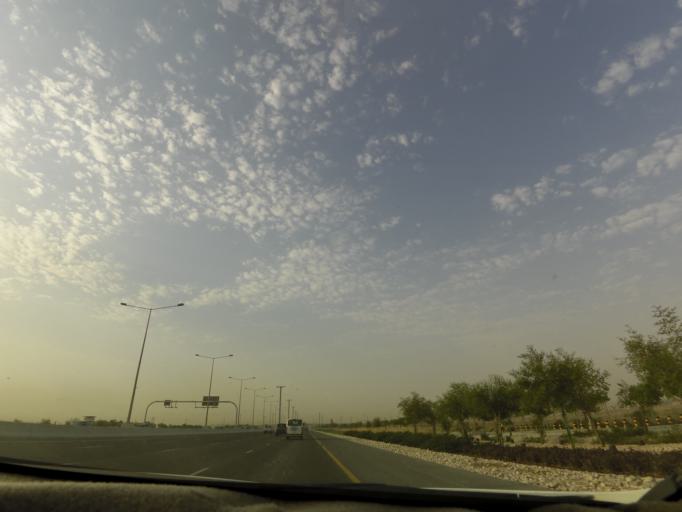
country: QA
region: Baladiyat ad Dawhah
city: Doha
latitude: 25.2498
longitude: 51.5871
